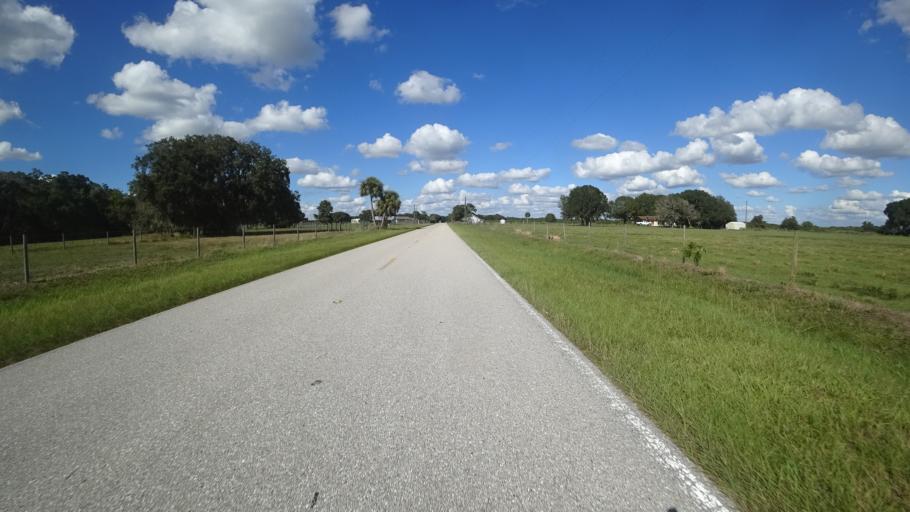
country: US
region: Florida
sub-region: Sarasota County
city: North Port
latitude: 27.2028
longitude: -82.1222
